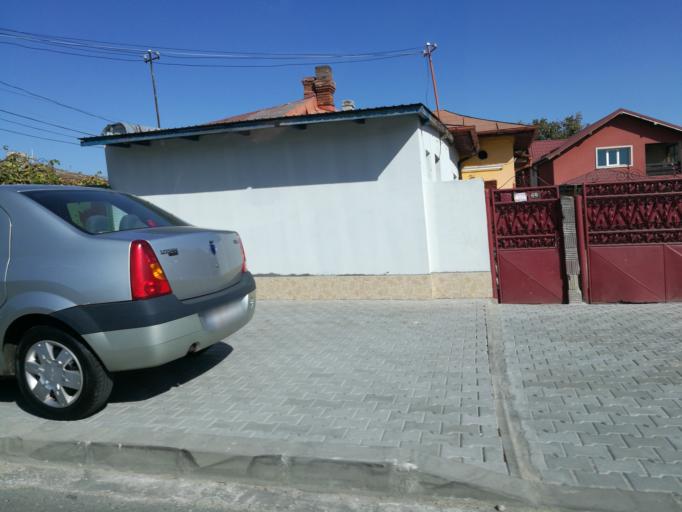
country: RO
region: Ilfov
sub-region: Comuna Dragomiresti-Vale
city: Dragomiresti-Deal
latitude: 44.4594
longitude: 25.9467
